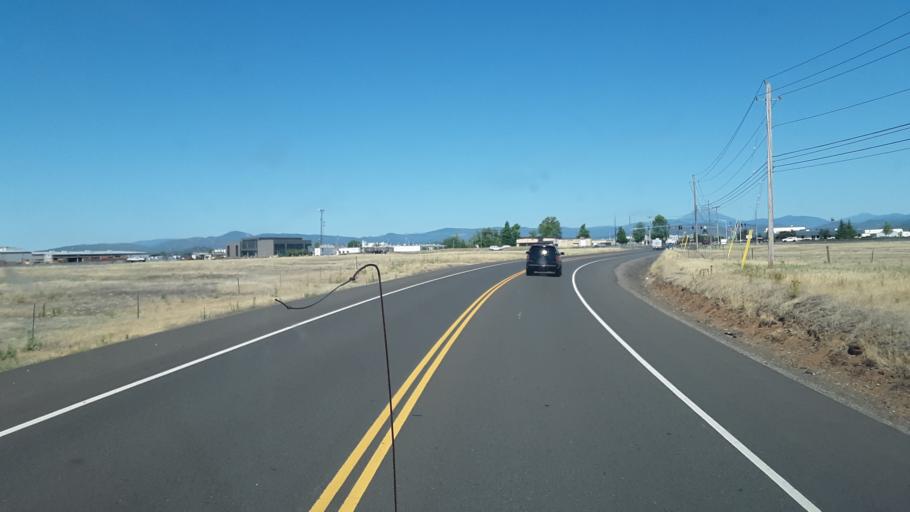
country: US
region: Oregon
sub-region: Jackson County
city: White City
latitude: 42.4271
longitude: -122.8895
